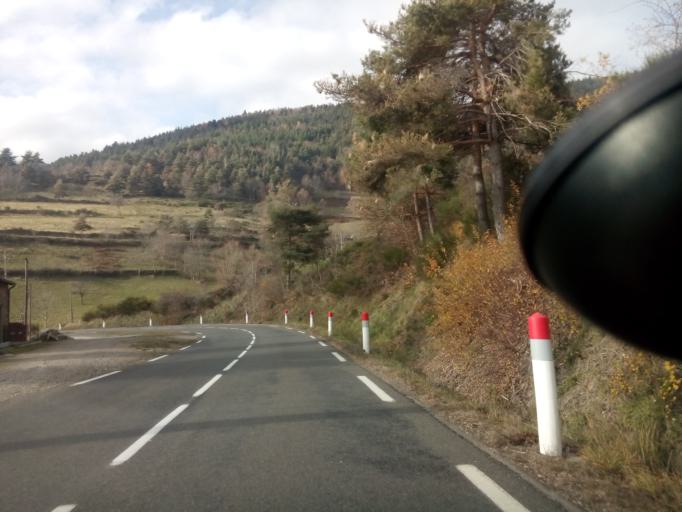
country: FR
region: Rhone-Alpes
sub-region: Departement de la Loire
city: Bourg-Argental
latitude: 45.3068
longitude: 4.5781
